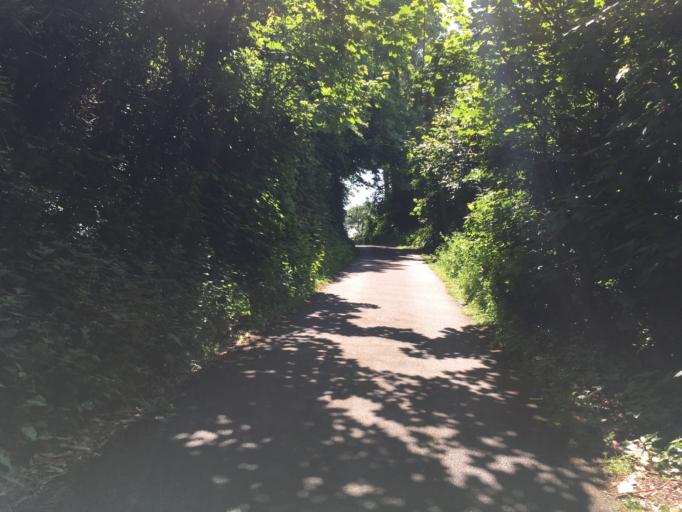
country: GB
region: England
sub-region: Devon
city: Dartmouth
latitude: 50.3441
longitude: -3.5618
